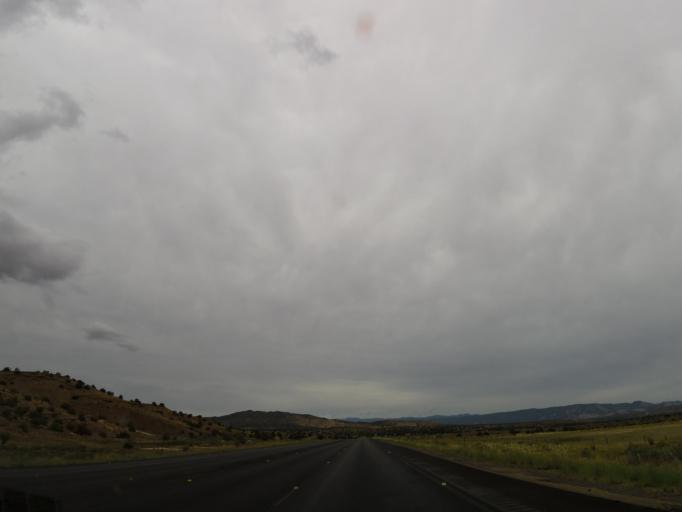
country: US
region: New Mexico
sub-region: Sandoval County
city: Jemez Pueblo
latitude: 35.5456
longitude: -106.8277
